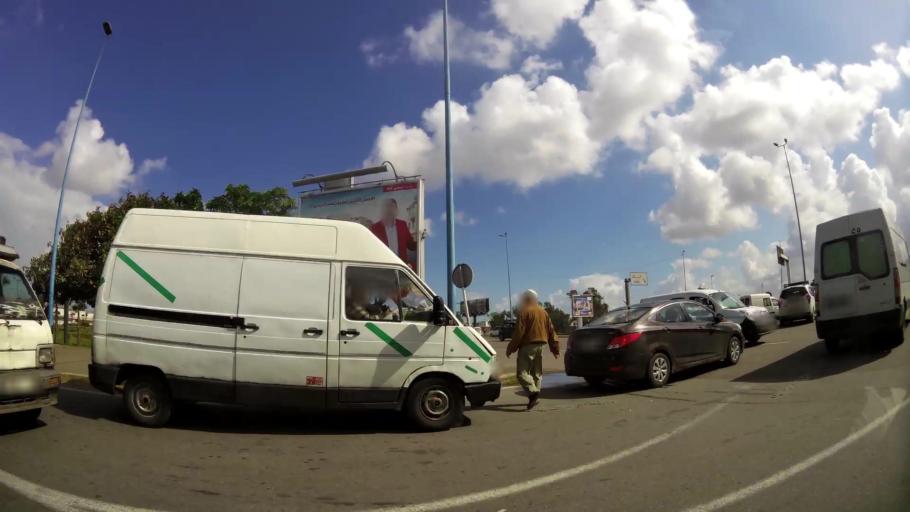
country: MA
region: Grand Casablanca
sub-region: Casablanca
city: Casablanca
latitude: 33.5586
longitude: -7.5945
